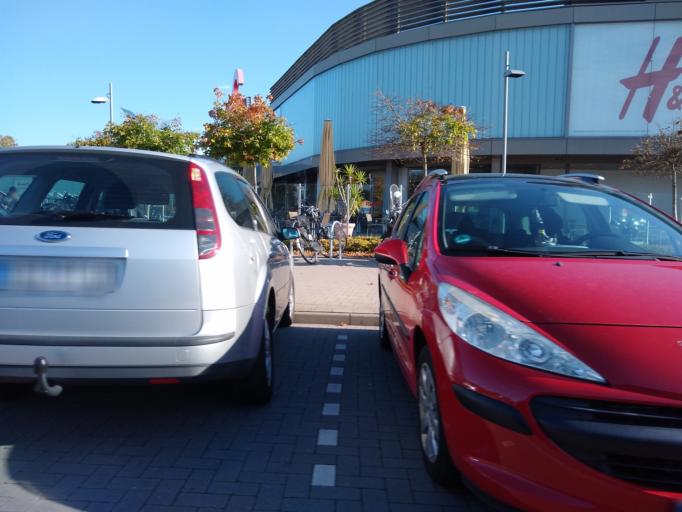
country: DE
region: Lower Saxony
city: Oldenburg
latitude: 53.1592
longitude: 8.1742
